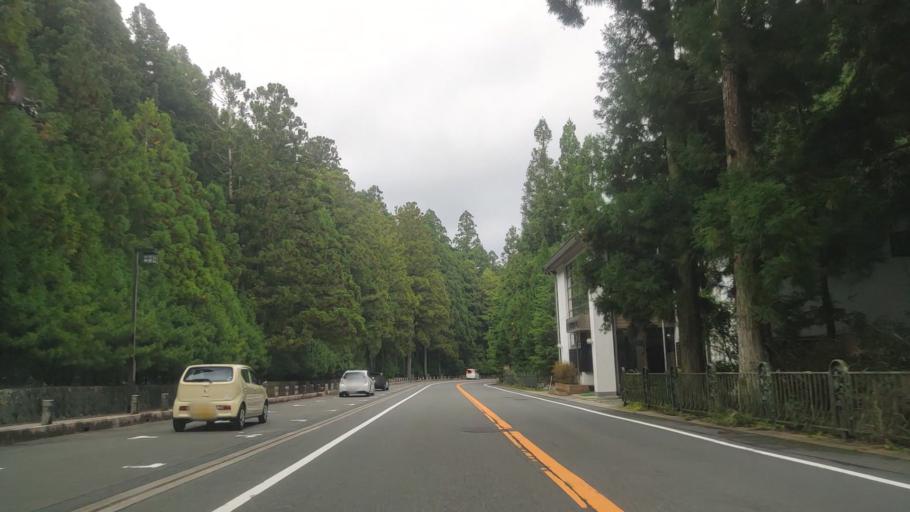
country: JP
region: Wakayama
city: Koya
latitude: 34.2161
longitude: 135.5990
